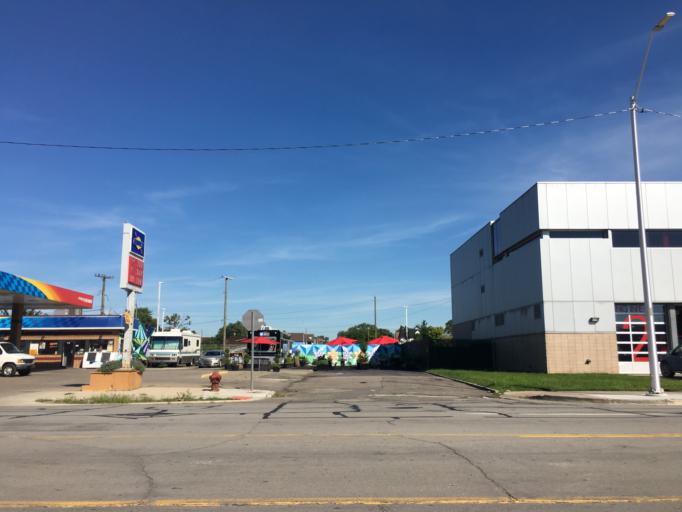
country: US
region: Michigan
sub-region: Wayne County
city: Detroit
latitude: 42.3106
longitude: -83.0939
